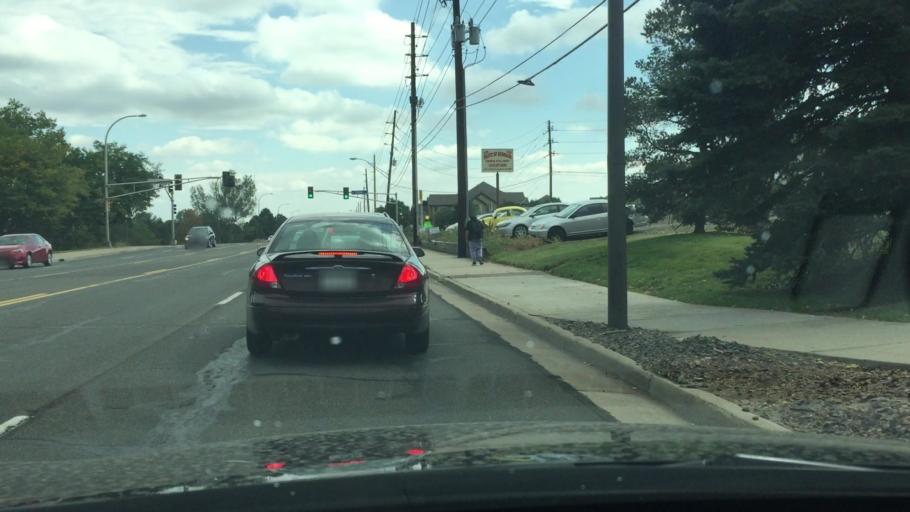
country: US
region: Colorado
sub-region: Jefferson County
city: Lakewood
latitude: 39.6821
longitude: -105.1107
